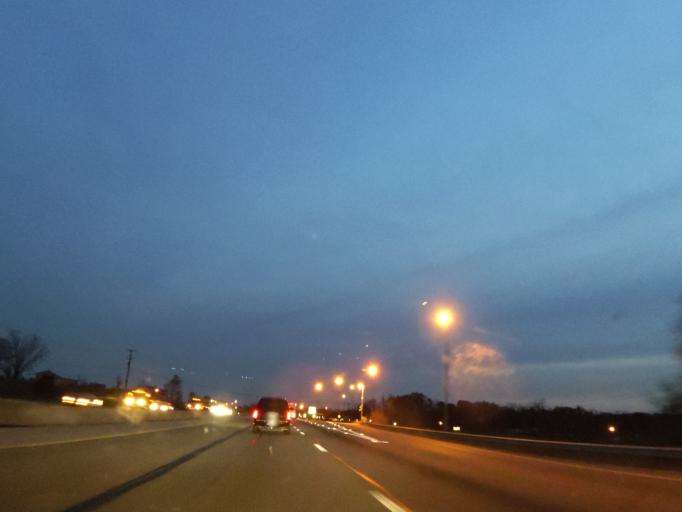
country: US
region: Kentucky
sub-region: Laurel County
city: London
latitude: 37.0521
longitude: -84.0986
